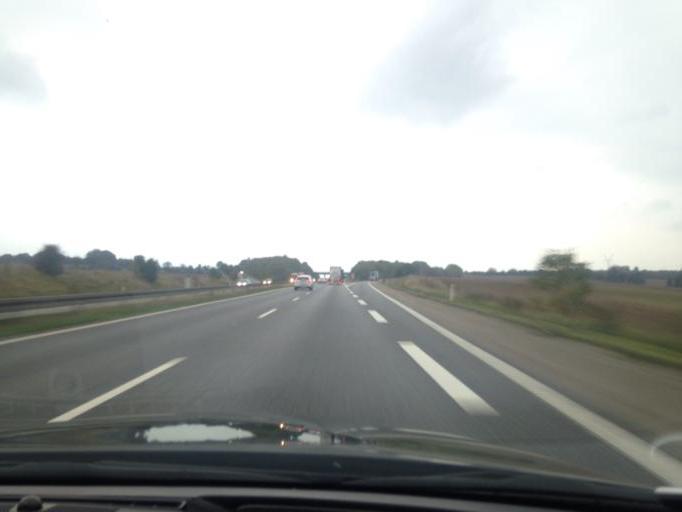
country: DK
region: South Denmark
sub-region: Kolding Kommune
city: Christiansfeld
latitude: 55.3555
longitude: 9.4473
